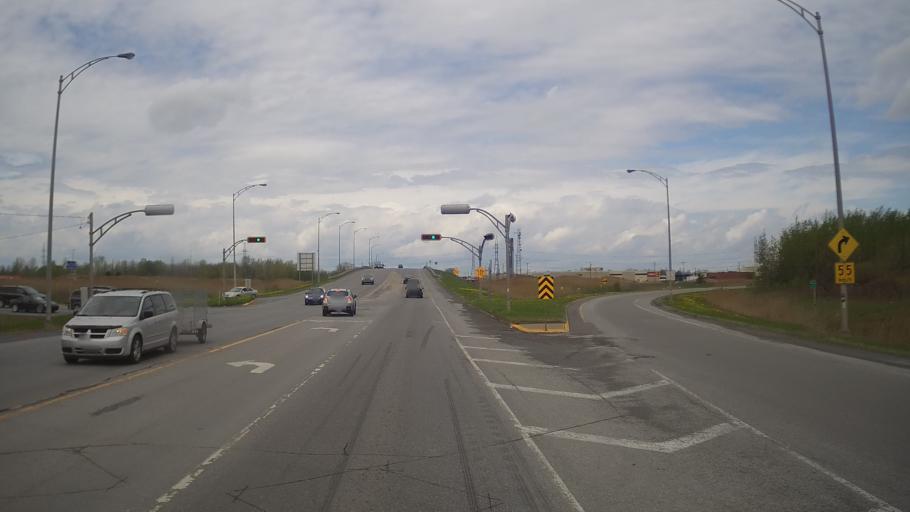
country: CA
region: Quebec
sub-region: Monteregie
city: La Prairie
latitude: 45.4021
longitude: -73.4578
